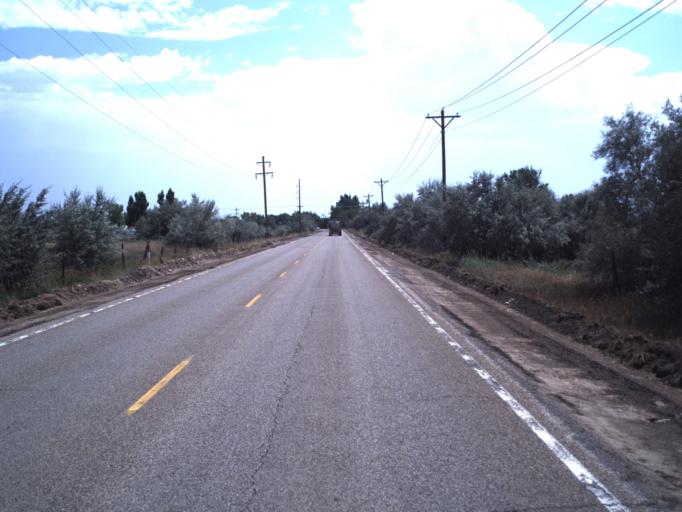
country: US
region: Utah
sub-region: Duchesne County
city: Roosevelt
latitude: 40.3554
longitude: -110.0297
